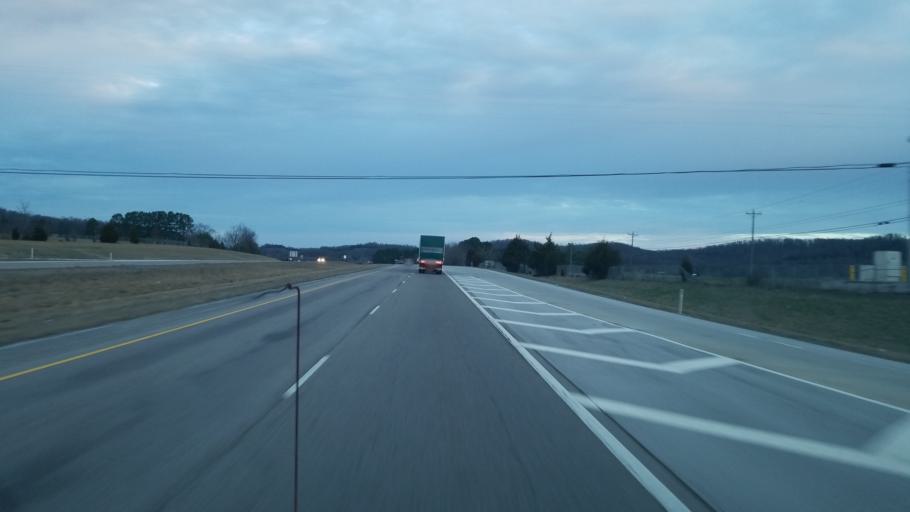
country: US
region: Tennessee
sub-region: White County
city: Sparta
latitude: 35.9686
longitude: -85.4869
